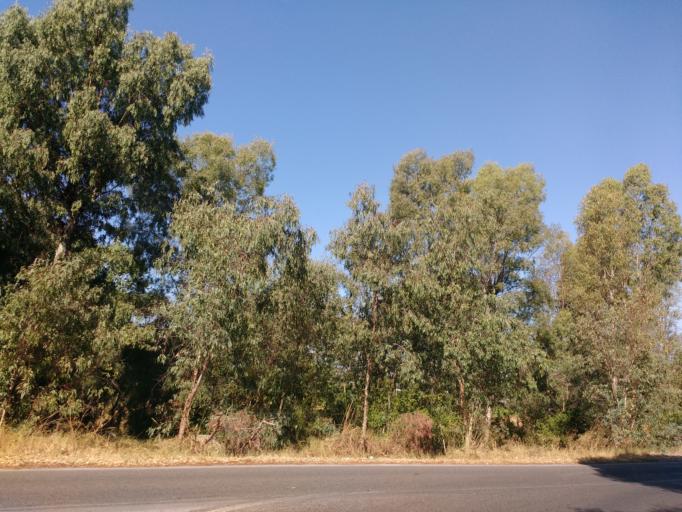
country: IT
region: Latium
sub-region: Citta metropolitana di Roma Capitale
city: Acilia-Castel Fusano-Ostia Antica
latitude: 41.7444
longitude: 12.3203
